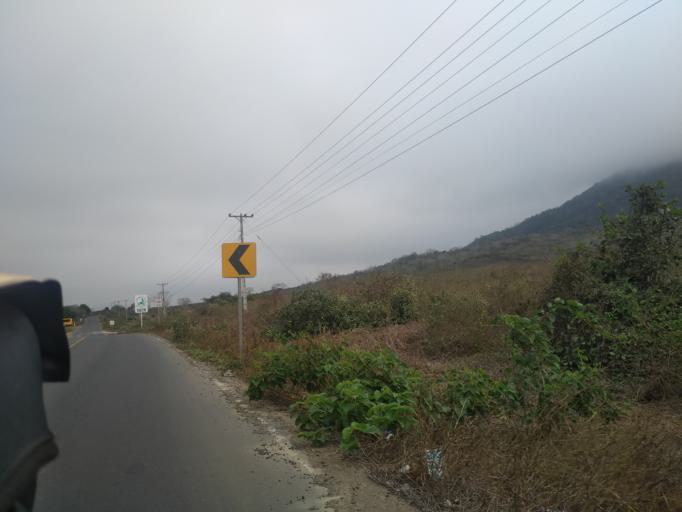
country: EC
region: Manabi
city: Montecristi
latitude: -1.0612
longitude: -80.6552
